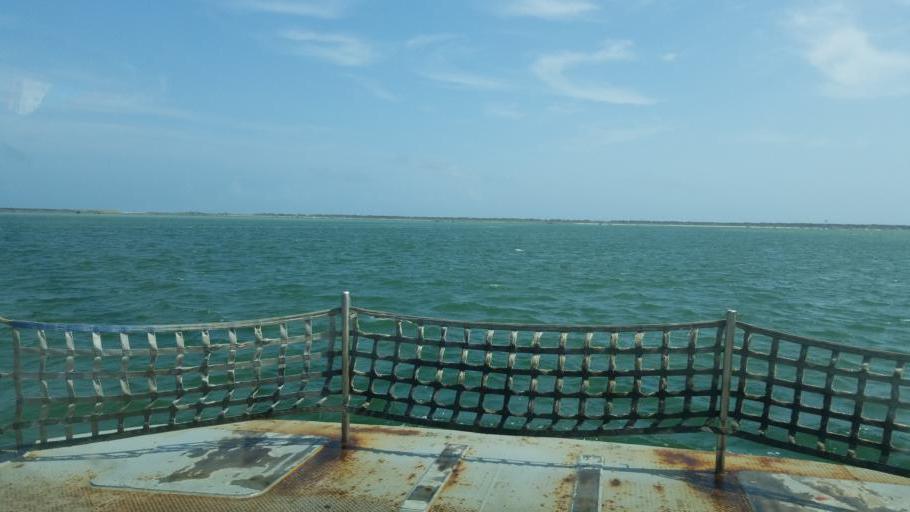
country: US
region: North Carolina
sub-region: Dare County
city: Buxton
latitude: 35.2094
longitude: -75.7327
